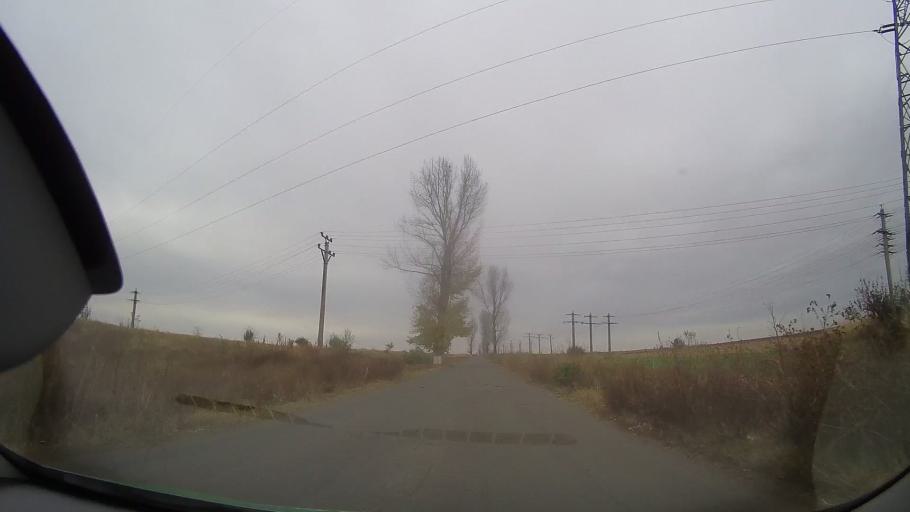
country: RO
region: Braila
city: Dudesti
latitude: 44.8983
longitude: 27.4329
